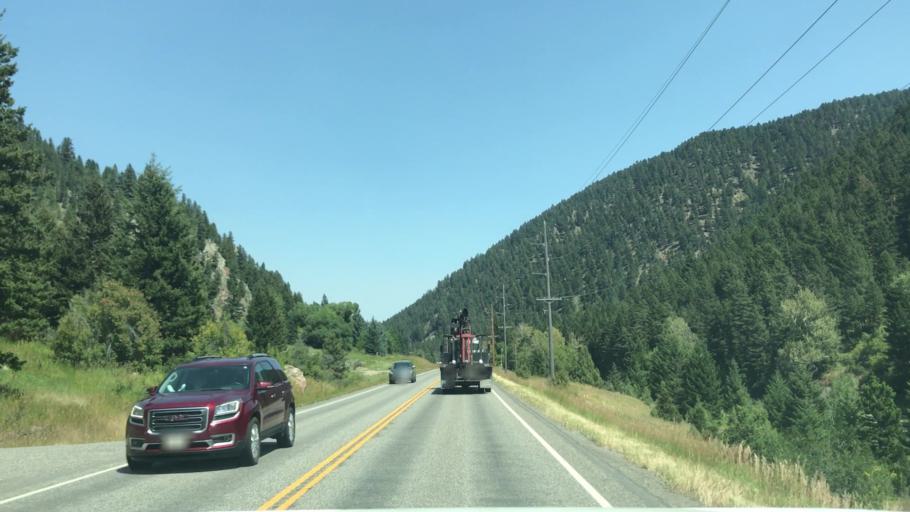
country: US
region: Montana
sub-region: Gallatin County
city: Four Corners
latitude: 45.5059
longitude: -111.2653
